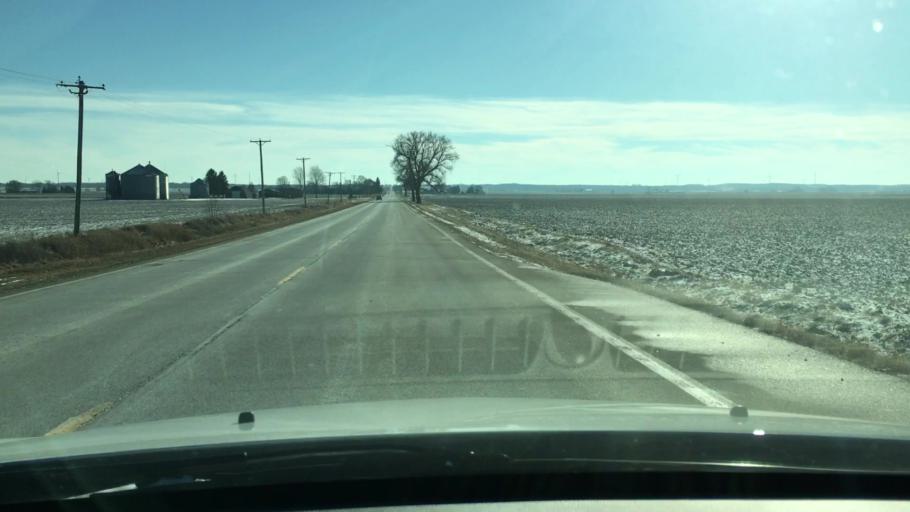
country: US
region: Illinois
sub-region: Ogle County
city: Rochelle
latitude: 41.7712
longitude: -89.0837
